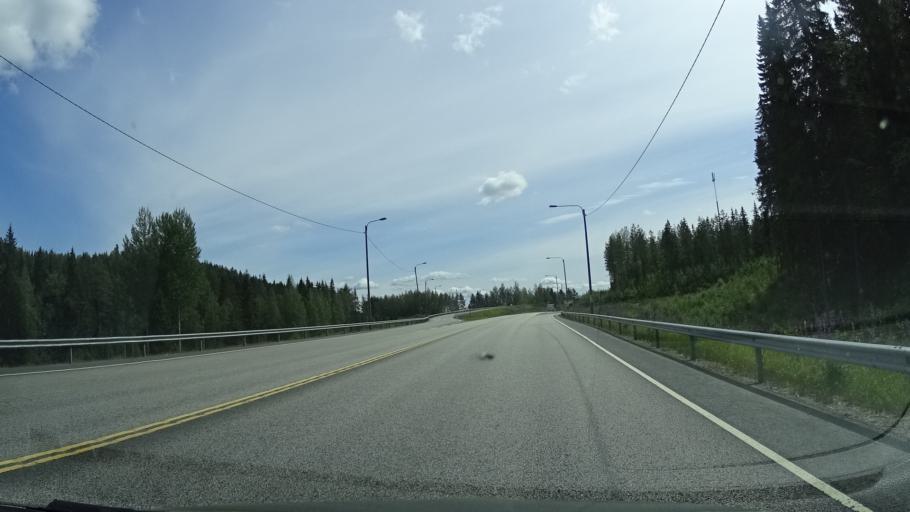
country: FI
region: Central Finland
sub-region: Jyvaeskylae
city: Jyvaeskylae
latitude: 62.2512
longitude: 25.6442
